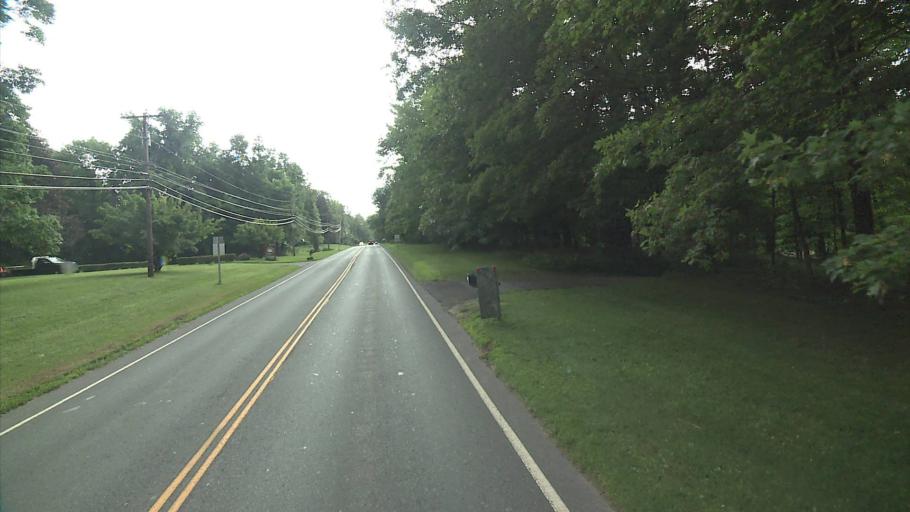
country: US
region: Connecticut
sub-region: New Haven County
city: Southbury
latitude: 41.4961
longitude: -73.2132
